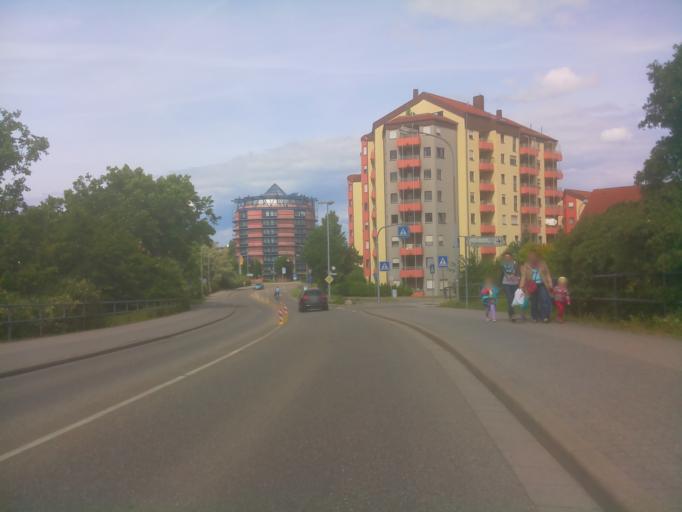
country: DE
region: Rheinland-Pfalz
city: Frankenthal
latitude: 49.5280
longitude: 8.3501
